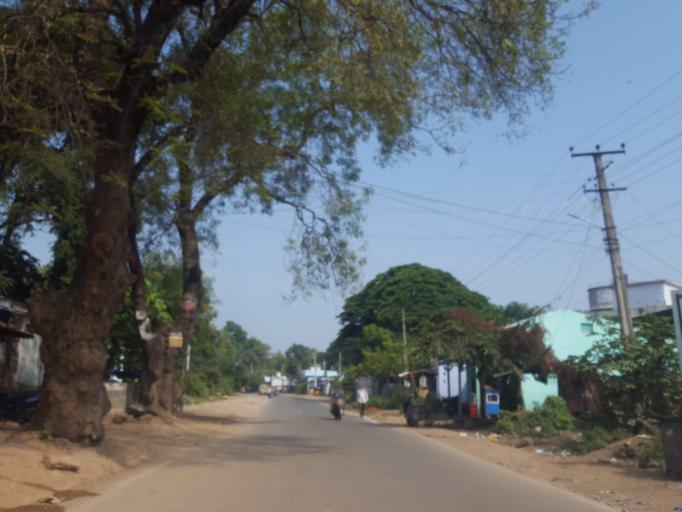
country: IN
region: Telangana
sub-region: Khammam
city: Yellandu
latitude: 17.5949
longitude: 80.3187
